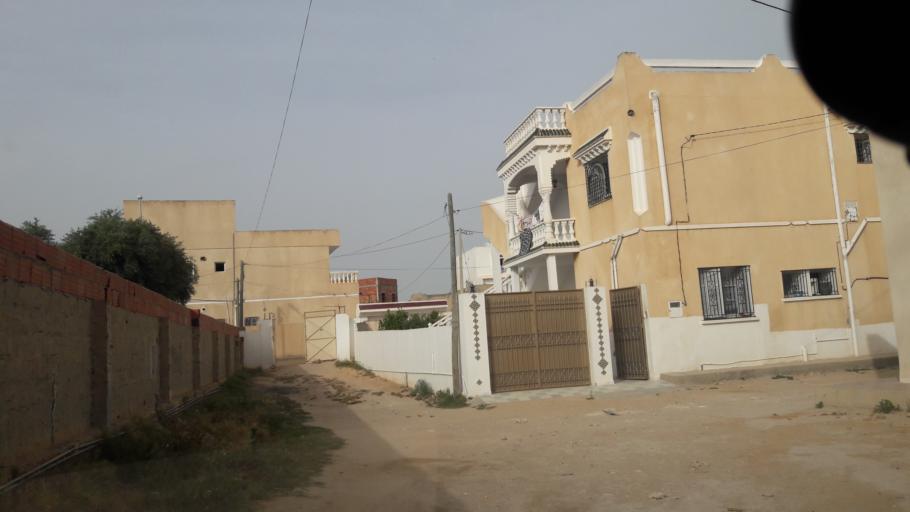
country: TN
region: Safaqis
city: Al Qarmadah
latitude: 34.7795
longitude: 10.7723
